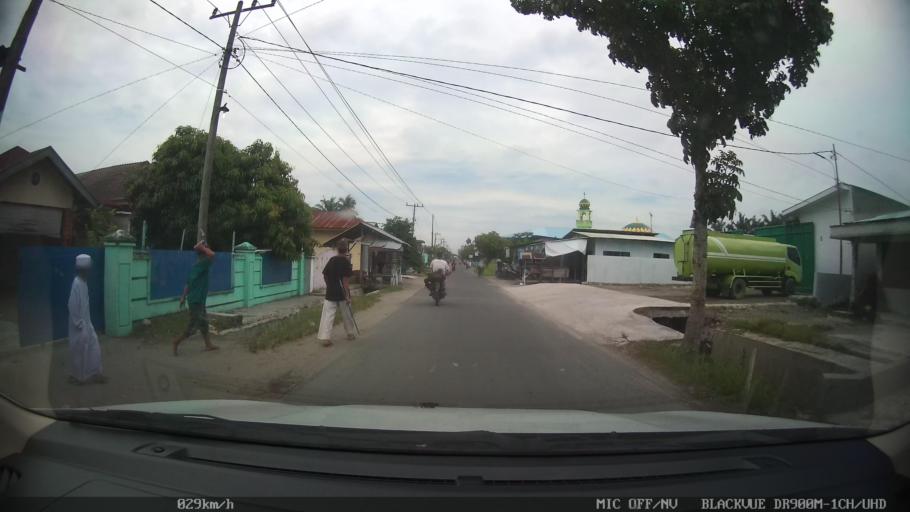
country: ID
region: North Sumatra
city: Binjai
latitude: 3.6337
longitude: 98.5537
